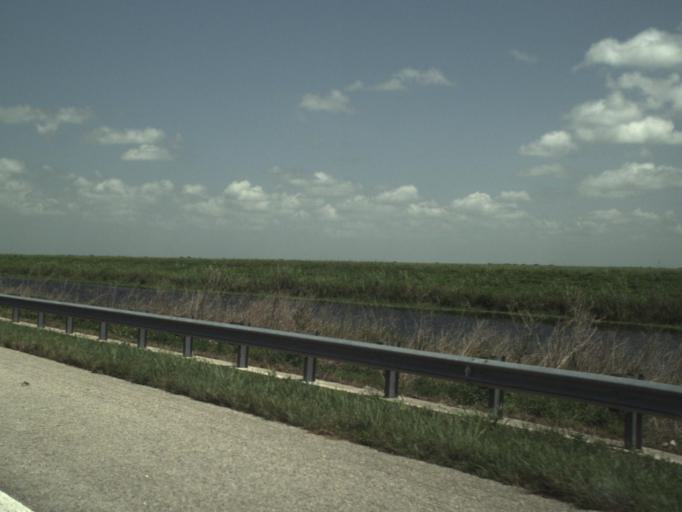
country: US
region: Florida
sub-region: Palm Beach County
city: Belle Glade Camp
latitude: 26.5158
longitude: -80.6777
